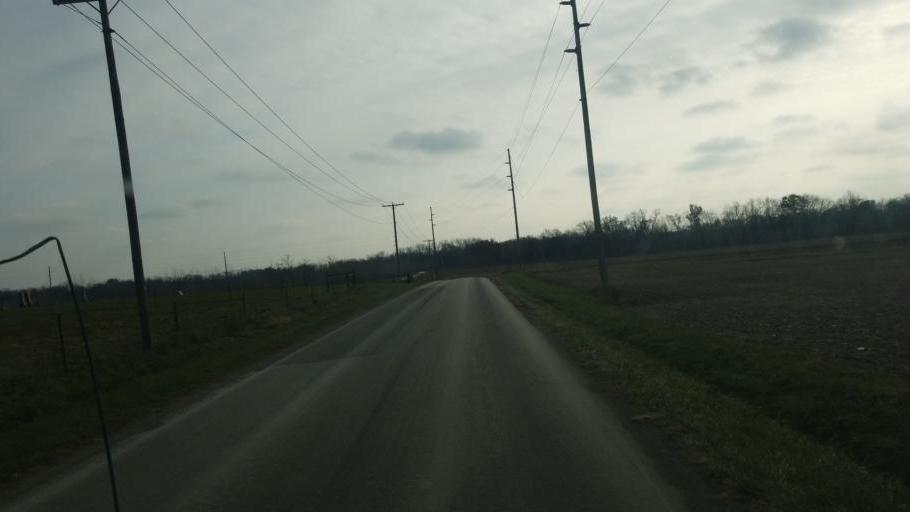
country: US
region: Indiana
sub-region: Adams County
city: Geneva
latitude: 40.6234
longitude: -84.9642
